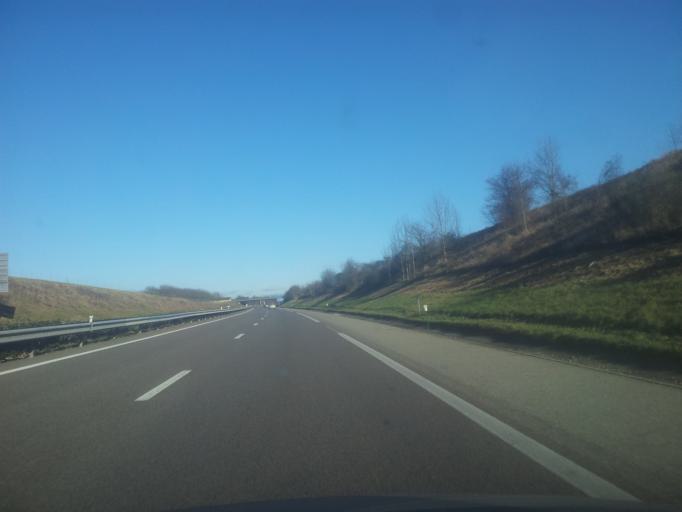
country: FR
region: Rhone-Alpes
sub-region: Departement de l'Isere
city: Saint-Marcellin
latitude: 45.1418
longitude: 5.3388
